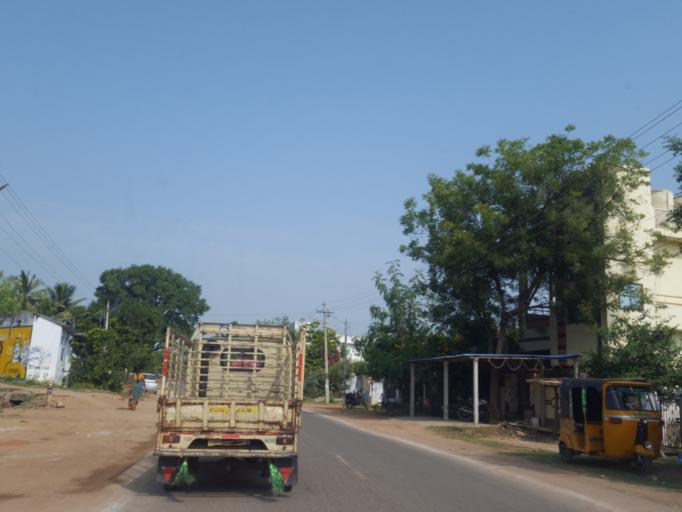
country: IN
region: Telangana
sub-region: Khammam
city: Yellandu
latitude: 17.6015
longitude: 80.3170
